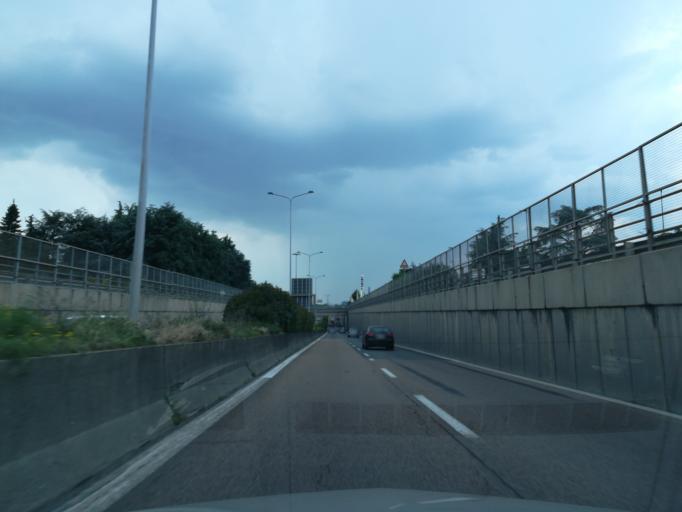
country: IT
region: Lombardy
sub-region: Provincia di Bergamo
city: Bergamo
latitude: 45.6762
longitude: 9.6638
